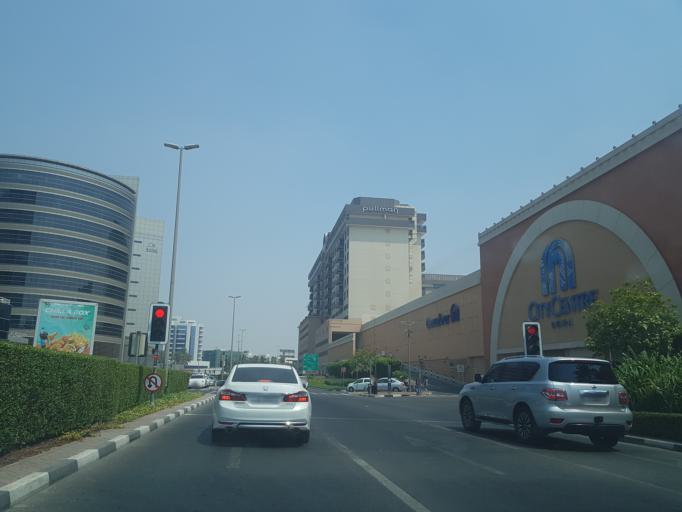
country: AE
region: Ash Shariqah
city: Sharjah
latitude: 25.2528
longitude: 55.3333
